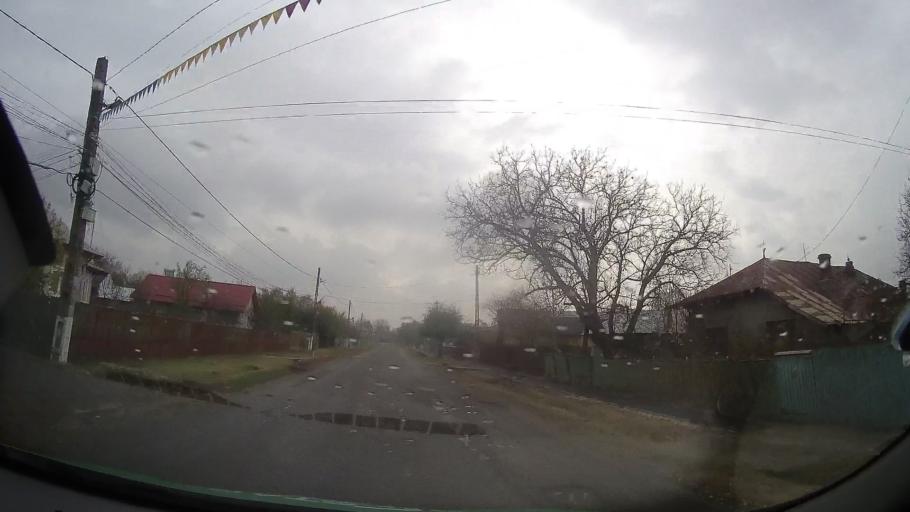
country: RO
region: Prahova
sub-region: Comuna Draganesti
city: Meri
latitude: 44.8434
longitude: 26.2688
